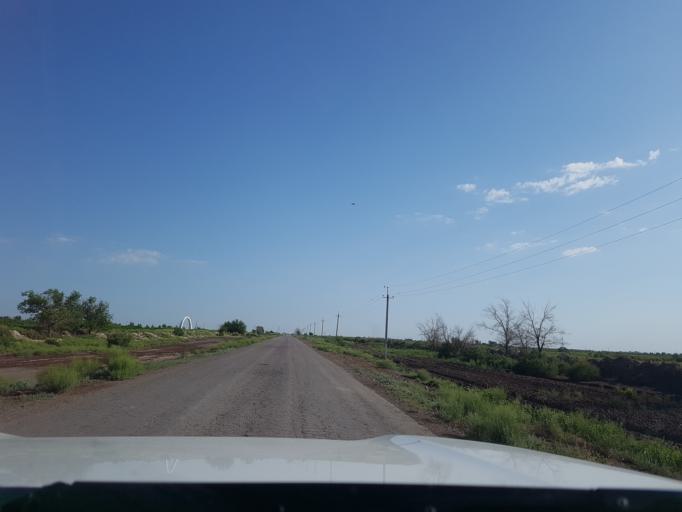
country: TM
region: Dasoguz
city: Koeneuergench
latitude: 41.8578
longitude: 58.7053
